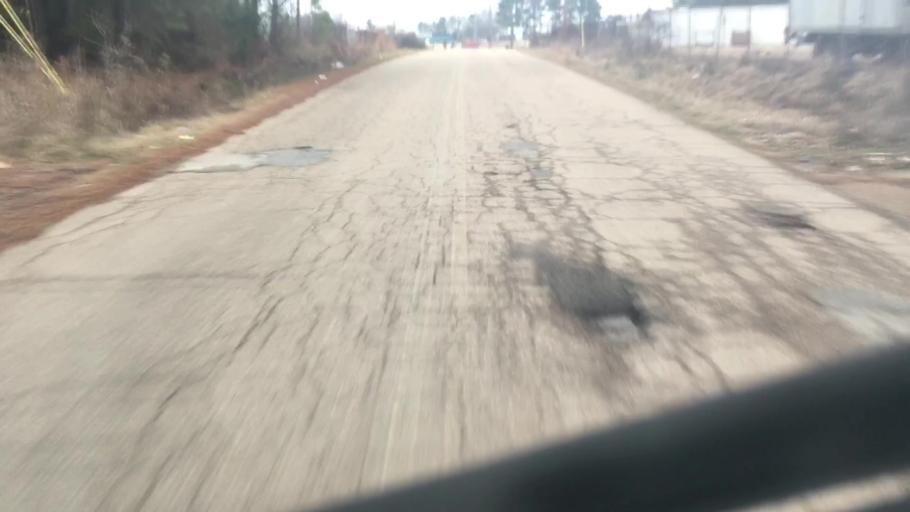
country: US
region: Alabama
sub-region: Walker County
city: Jasper
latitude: 33.8342
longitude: -87.2254
